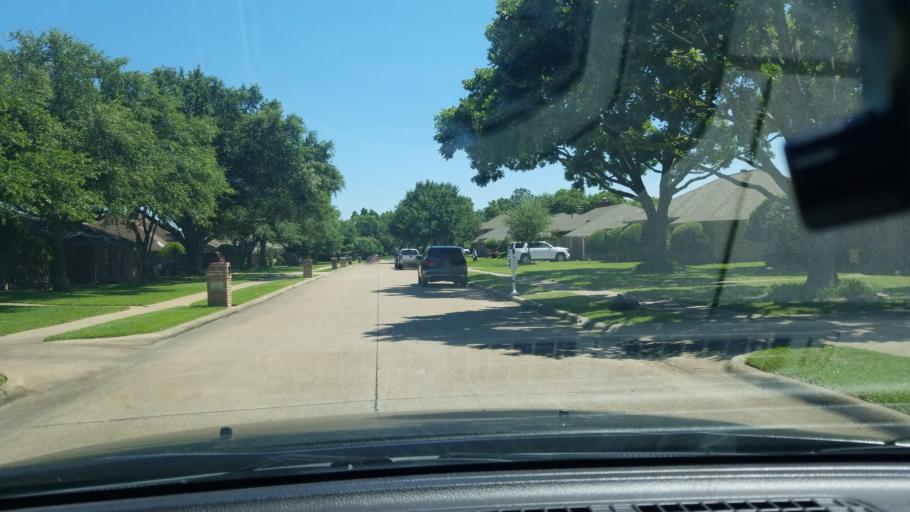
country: US
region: Texas
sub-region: Dallas County
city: Mesquite
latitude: 32.7576
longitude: -96.6021
